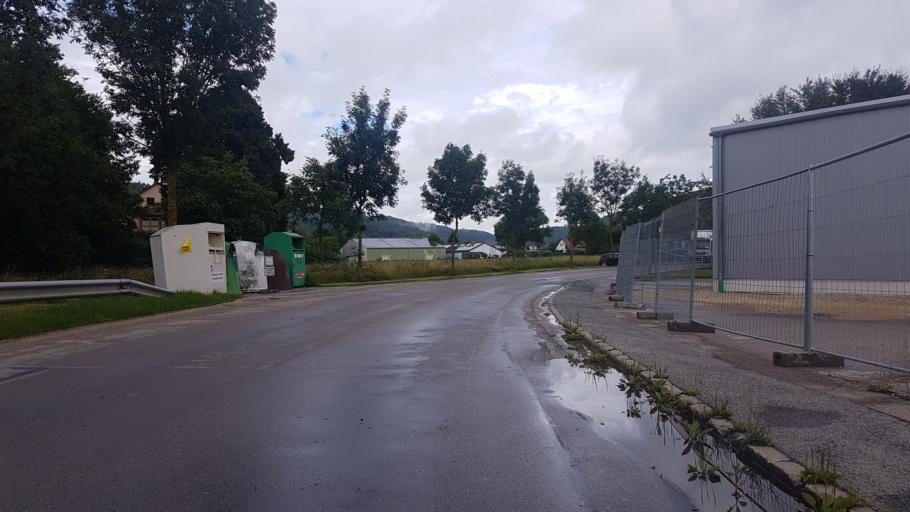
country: DE
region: Bavaria
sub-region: Upper Palatinate
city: Dietfurt
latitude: 49.0292
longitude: 11.5910
